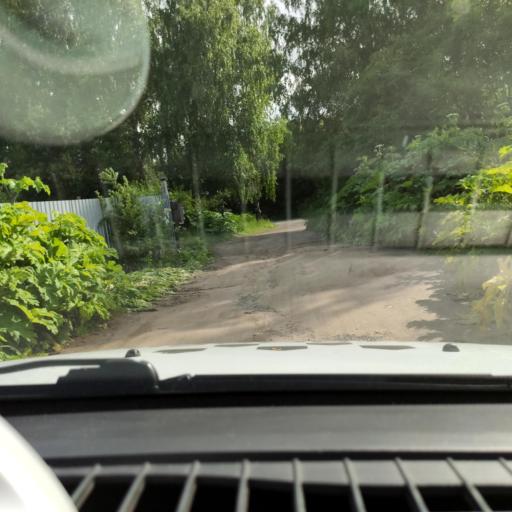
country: RU
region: Perm
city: Overyata
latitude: 58.0990
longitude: 55.8566
